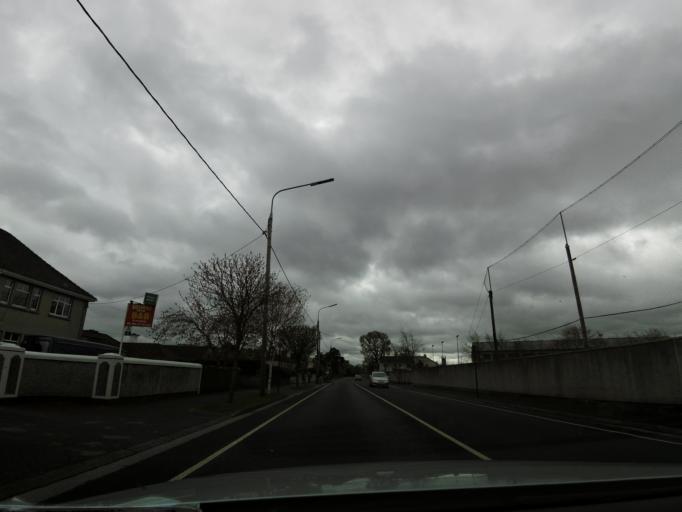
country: IE
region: Leinster
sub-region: Kilkenny
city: Kilkenny
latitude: 52.6619
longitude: -7.2608
